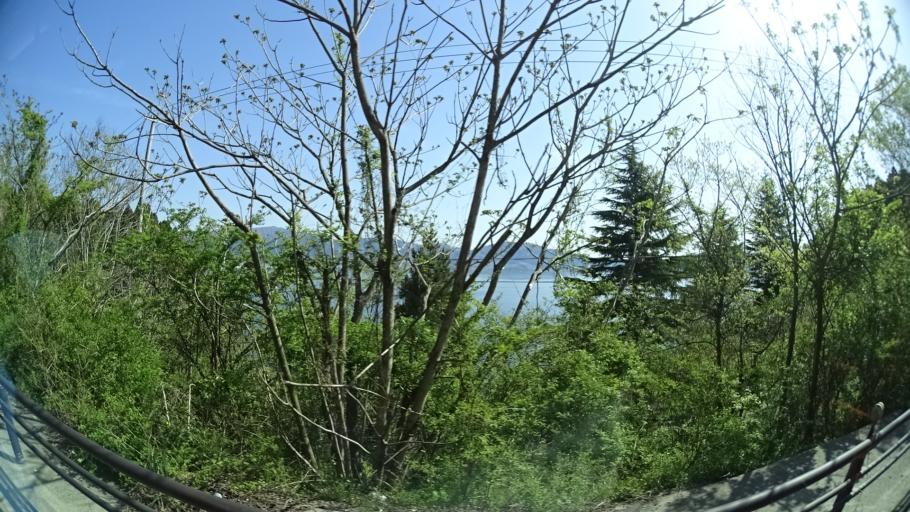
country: JP
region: Iwate
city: Ofunato
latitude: 38.9743
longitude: 141.6301
